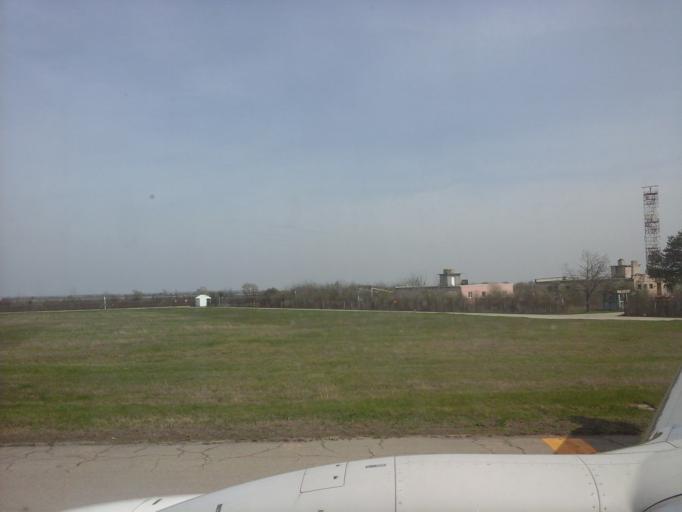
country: RO
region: Ilfov
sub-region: Comuna Otopeni
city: Otopeni
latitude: 44.5704
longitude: 26.1062
